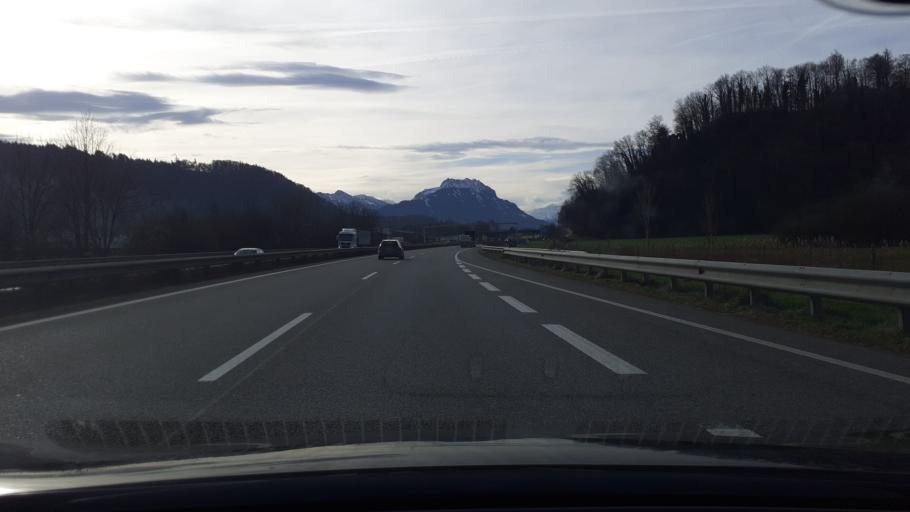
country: AT
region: Vorarlberg
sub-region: Politischer Bezirk Feldkirch
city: Gotzis
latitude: 47.3276
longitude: 9.6276
